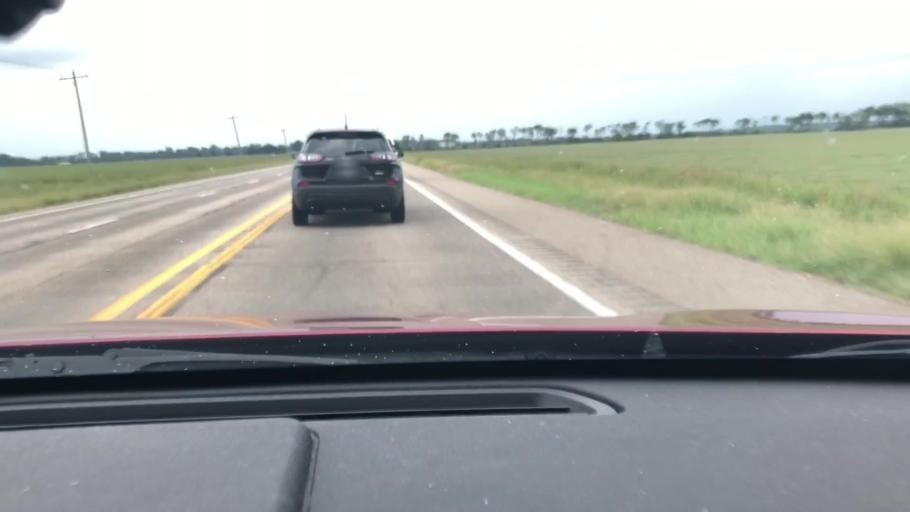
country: US
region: Arkansas
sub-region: Lafayette County
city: Lewisville
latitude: 33.3878
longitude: -93.7359
